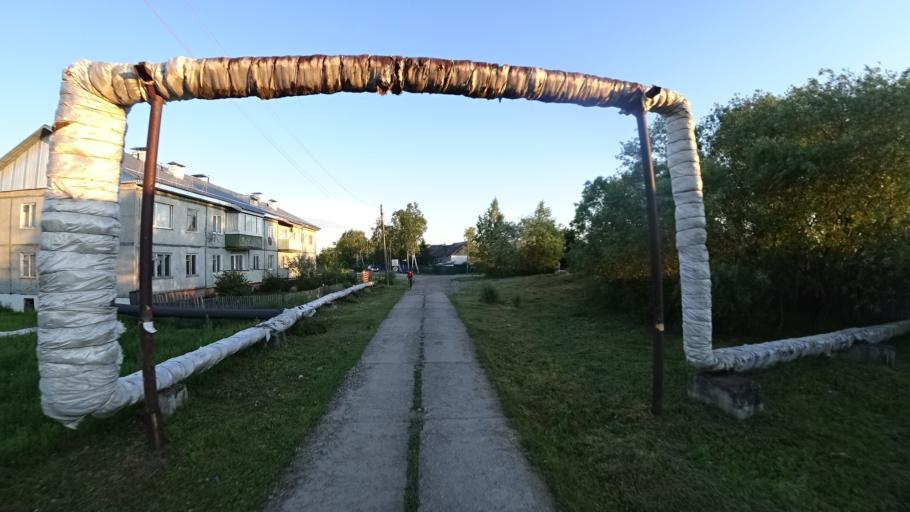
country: RU
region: Khabarovsk Krai
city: Khor
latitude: 47.8470
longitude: 134.9556
